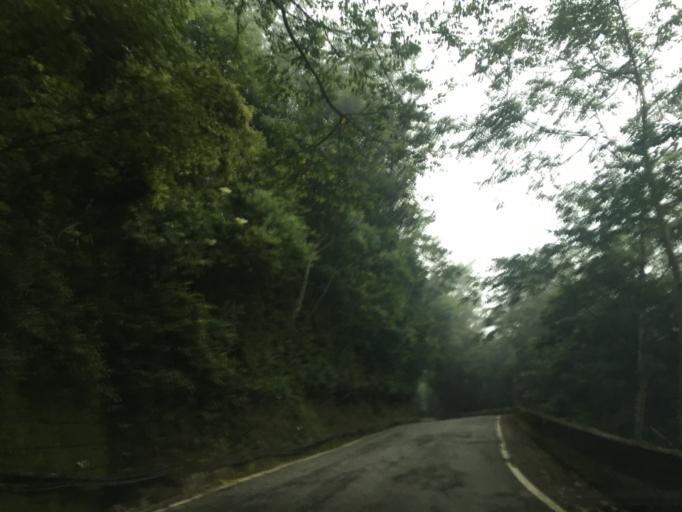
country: TW
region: Taiwan
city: Fengyuan
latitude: 24.2452
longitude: 120.9259
